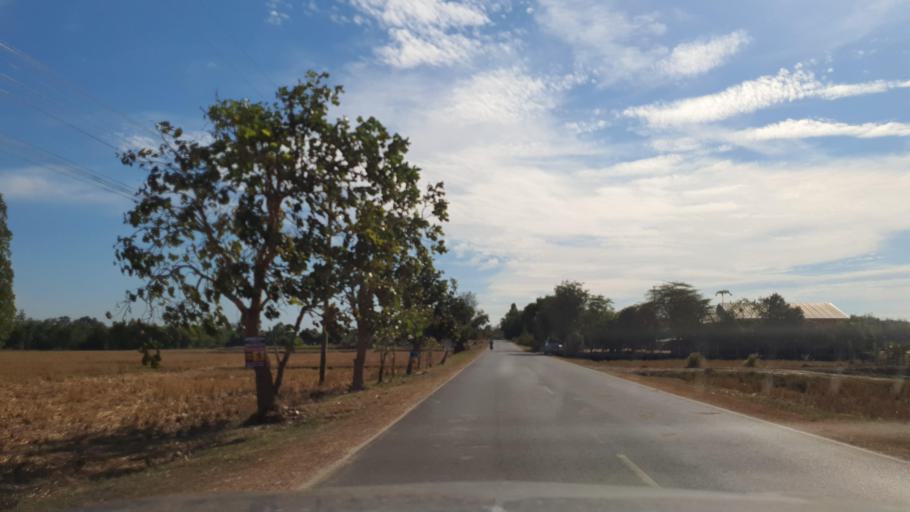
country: TH
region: Kalasin
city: Kuchinarai
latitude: 16.5510
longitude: 104.0969
